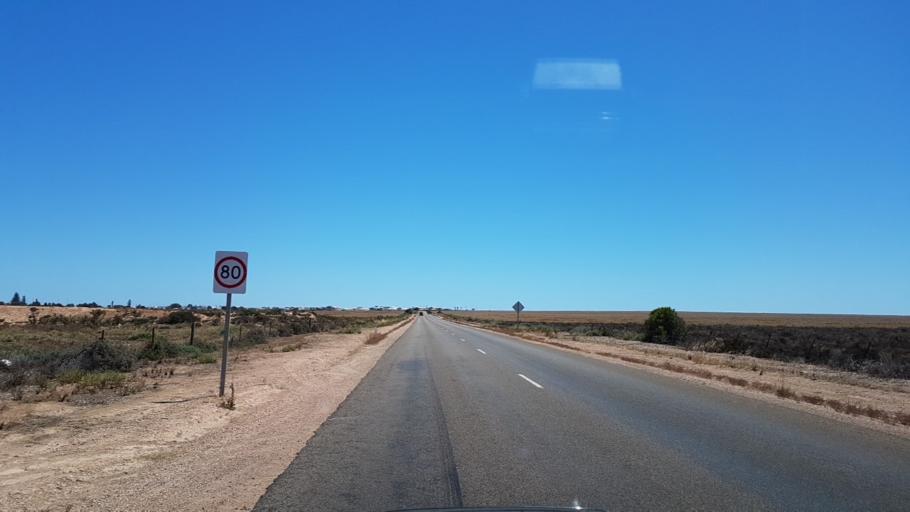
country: AU
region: South Australia
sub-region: Copper Coast
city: Wallaroo
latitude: -33.9070
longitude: 137.6400
